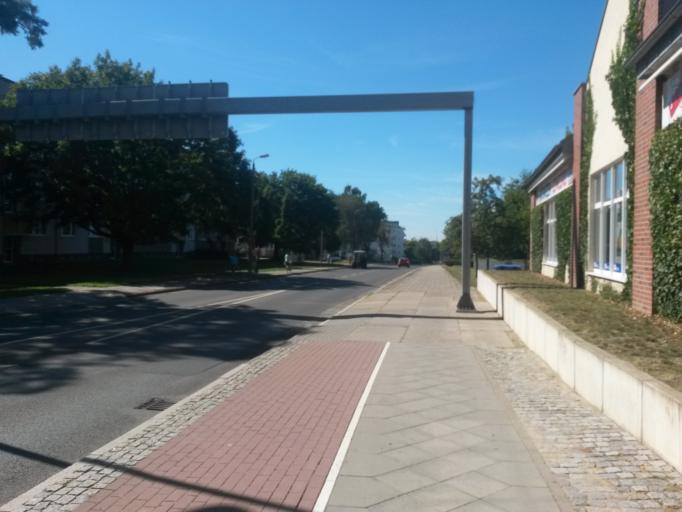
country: DE
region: Brandenburg
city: Prenzlau
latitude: 53.3170
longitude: 13.8600
